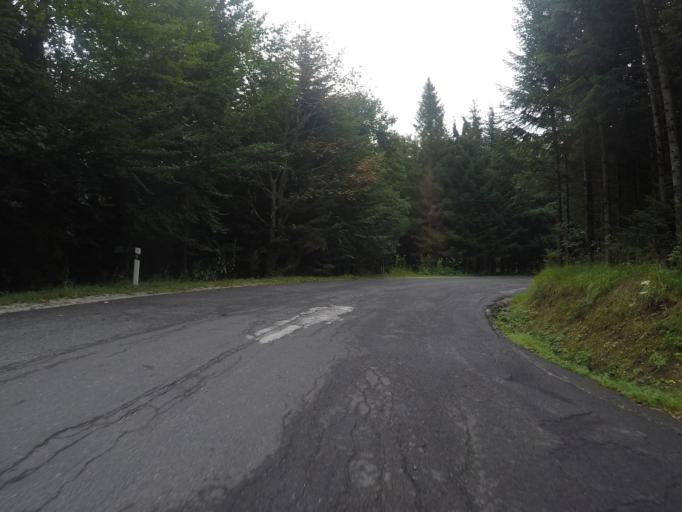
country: SK
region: Kosicky
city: Spisska Nova Ves
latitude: 48.8575
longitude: 20.5202
